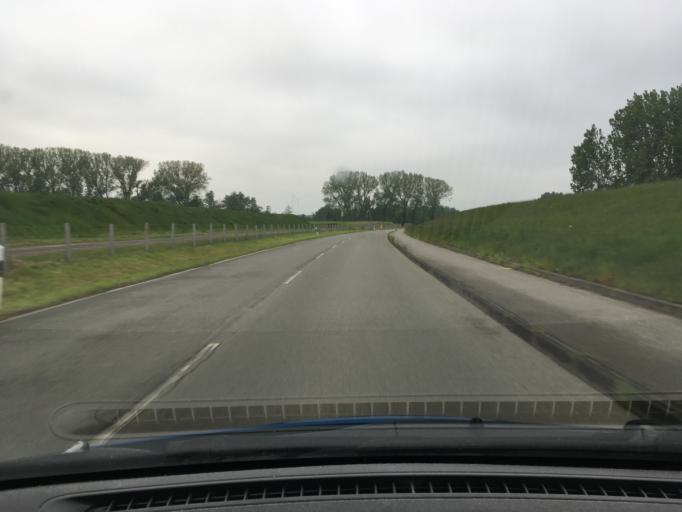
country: DE
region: Hamburg
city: Rothenburgsort
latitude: 53.4845
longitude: 10.0496
